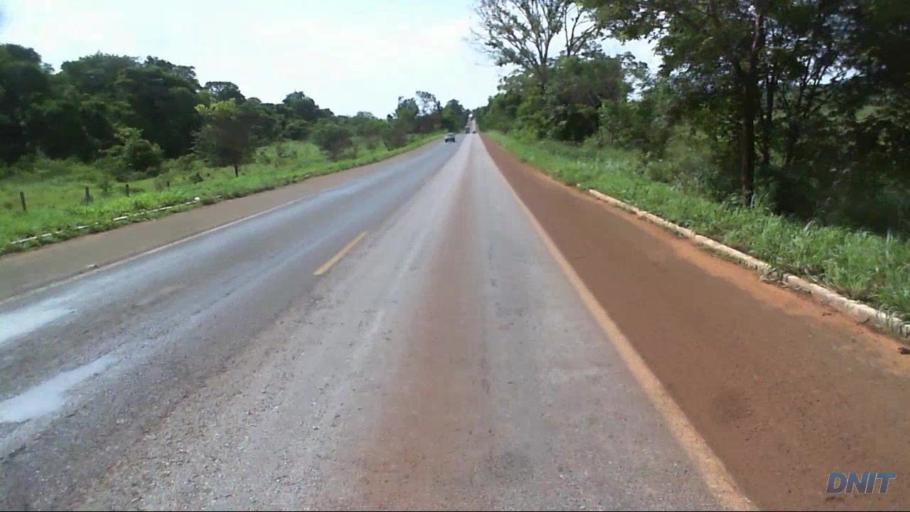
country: BR
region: Goias
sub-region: Barro Alto
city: Barro Alto
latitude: -15.0091
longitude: -48.9017
